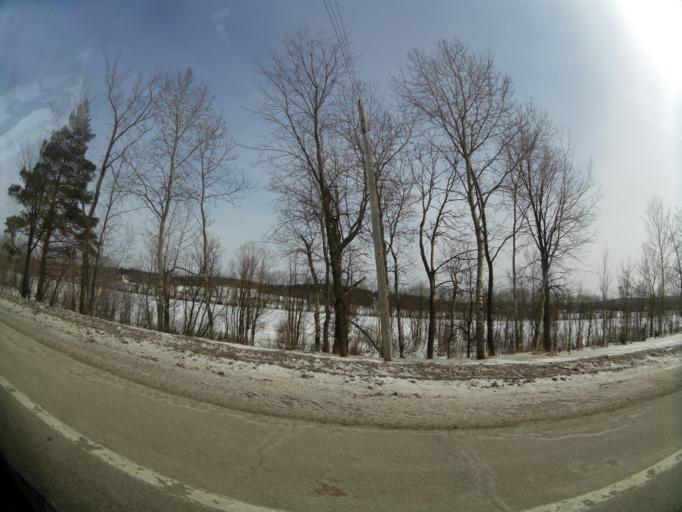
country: CA
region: Quebec
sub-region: Laurentides
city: Mont-Laurier
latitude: 46.5218
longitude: -75.4989
